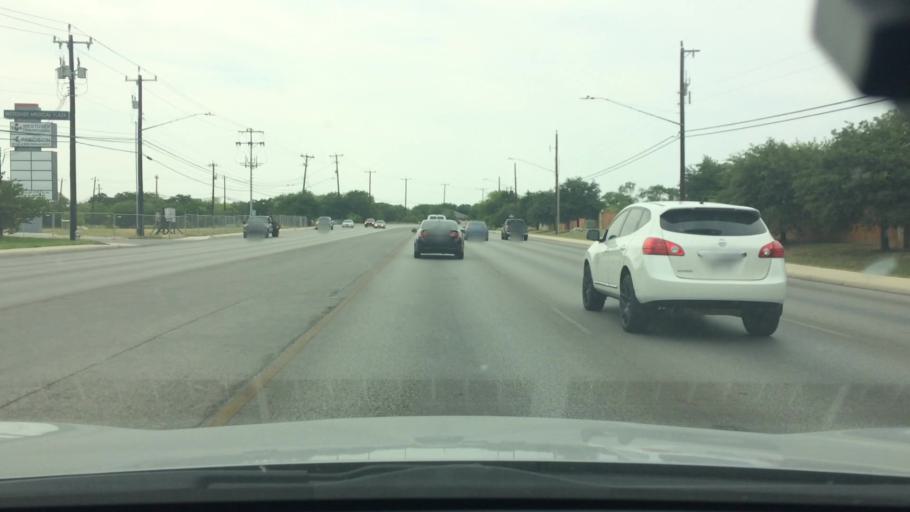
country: US
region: Texas
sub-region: Bexar County
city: Leon Valley
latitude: 29.4788
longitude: -98.6645
